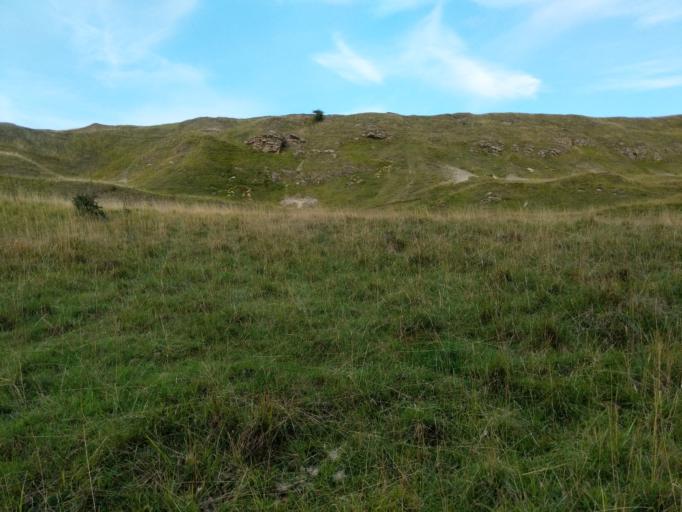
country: GB
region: England
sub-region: Gloucestershire
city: Gotherington
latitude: 51.9350
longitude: -2.0273
